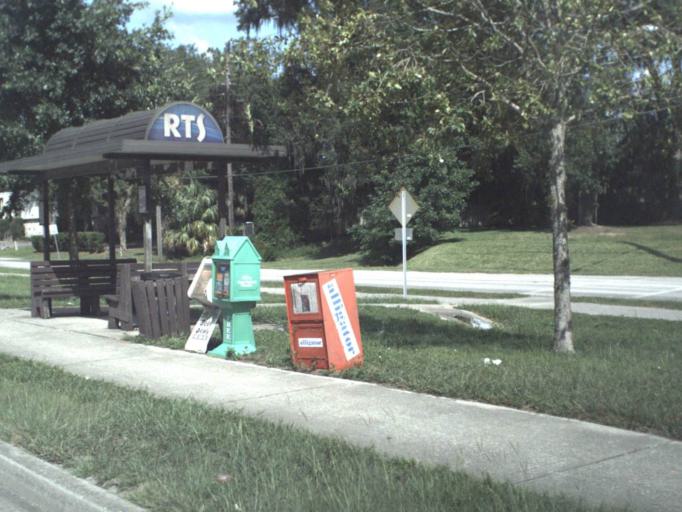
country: US
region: Florida
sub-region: Alachua County
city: Gainesville
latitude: 29.6297
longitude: -82.3669
